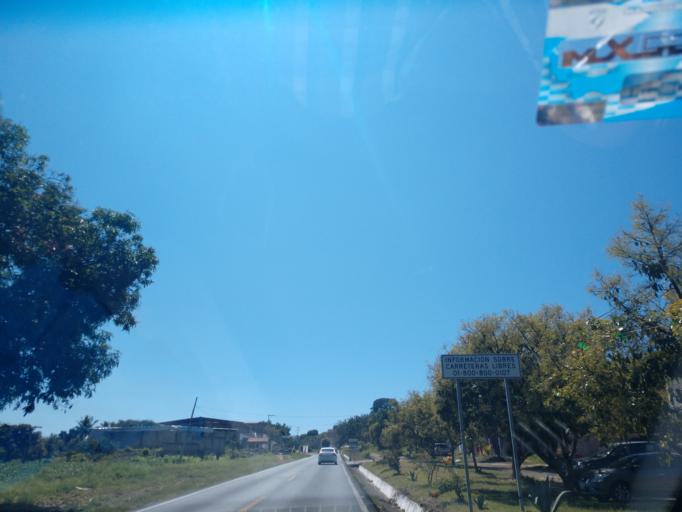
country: MX
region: Nayarit
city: Xalisco
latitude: 21.4119
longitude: -104.8972
